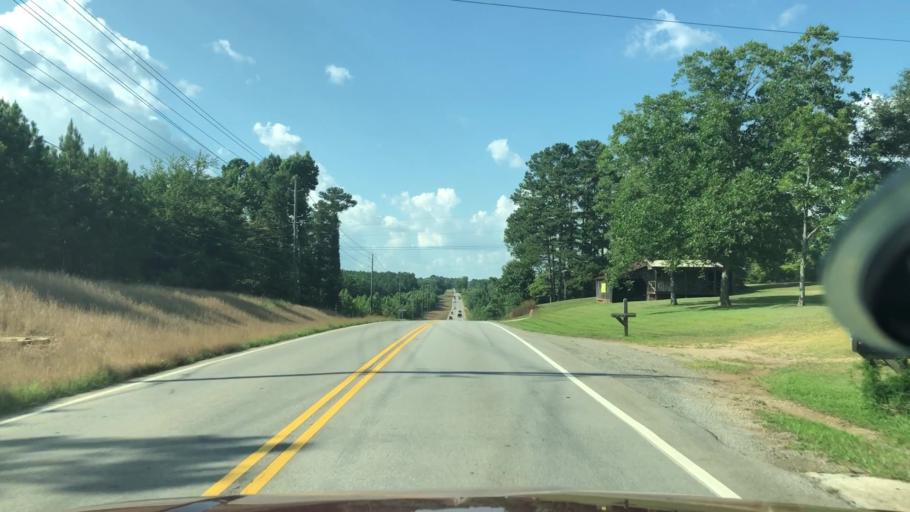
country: US
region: Georgia
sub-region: Paulding County
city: Dallas
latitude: 33.9948
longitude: -84.8697
